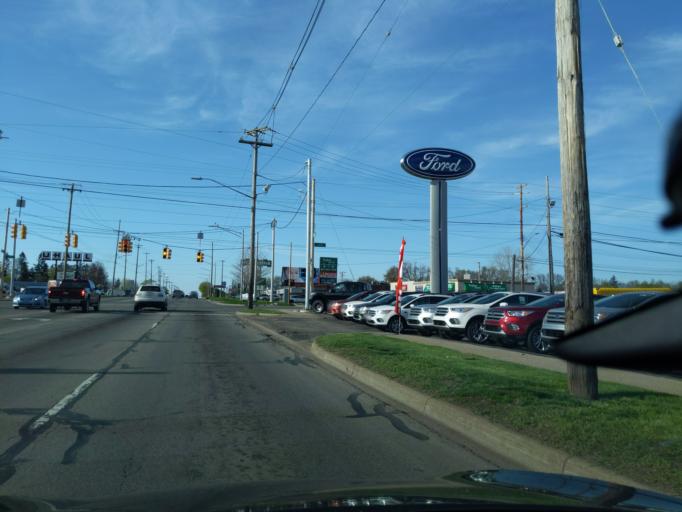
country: US
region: Michigan
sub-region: Ingham County
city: Lansing
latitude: 42.6825
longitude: -84.5480
